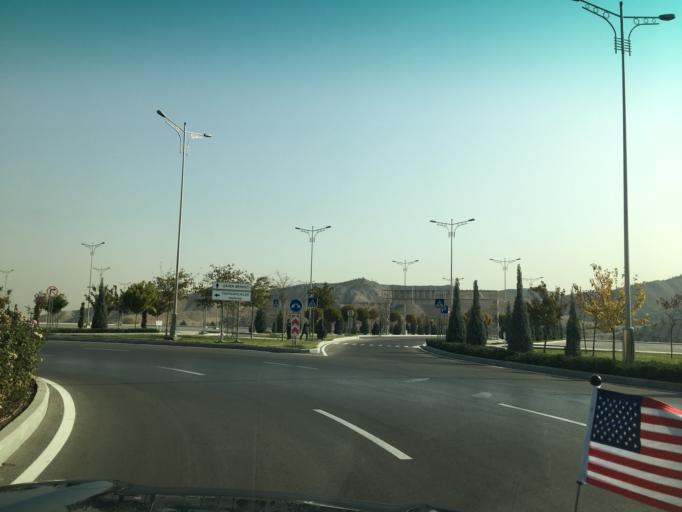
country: TM
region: Ahal
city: Ashgabat
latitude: 37.9361
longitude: 58.3217
